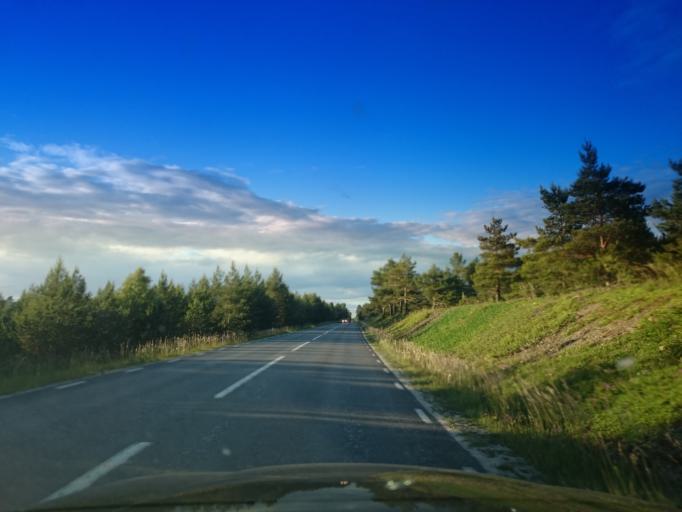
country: SE
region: Gotland
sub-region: Gotland
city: Hemse
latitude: 57.3402
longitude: 18.3784
